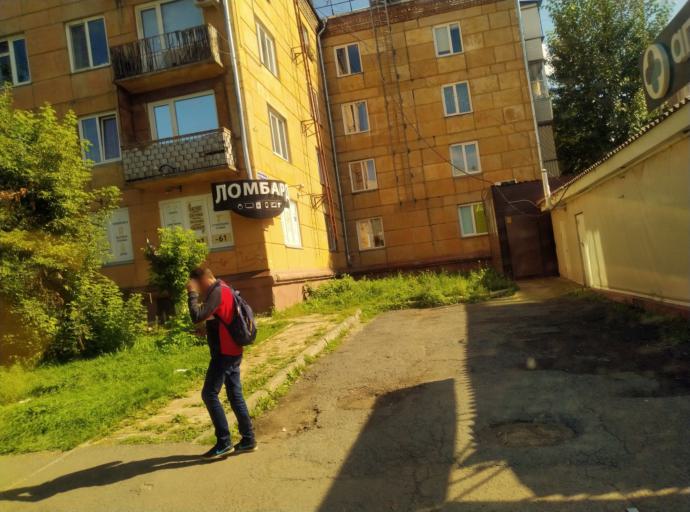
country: RU
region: Krasnoyarskiy
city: Krasnoyarsk
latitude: 55.9768
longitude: 92.8429
